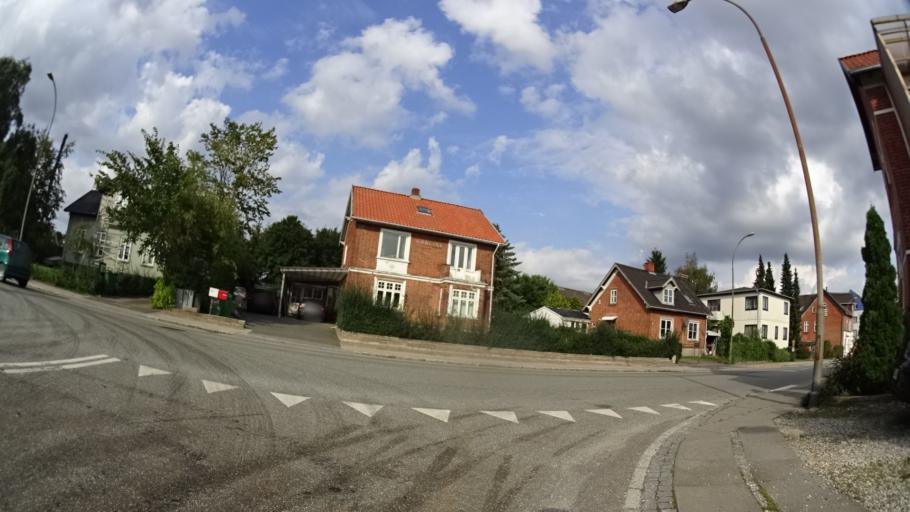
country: DK
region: Central Jutland
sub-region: Arhus Kommune
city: Stavtrup
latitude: 56.1533
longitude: 10.0999
